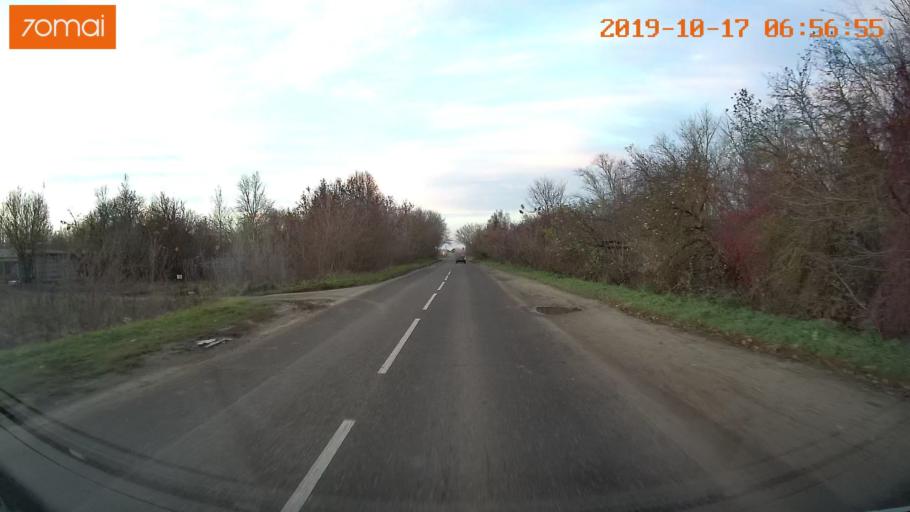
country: RU
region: Vladimir
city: Suzdal'
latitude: 56.4413
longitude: 40.4433
